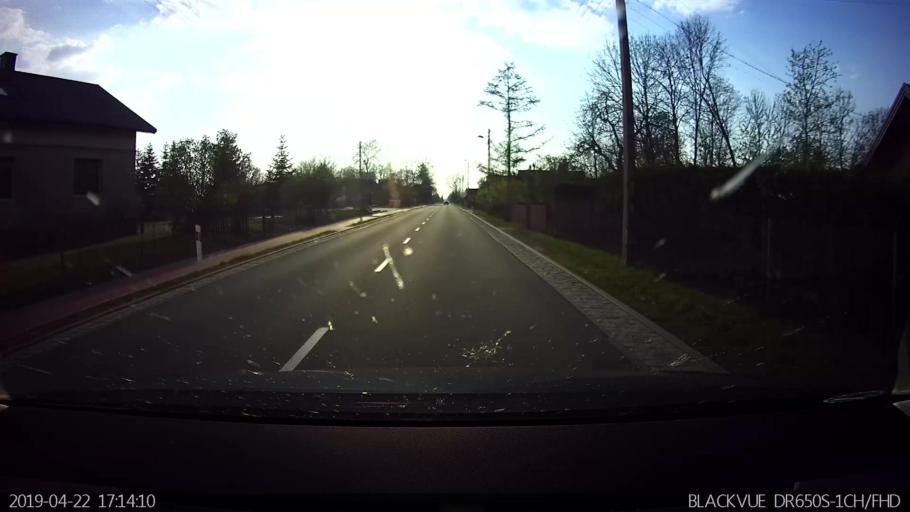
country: PL
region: Masovian Voivodeship
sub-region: Powiat sokolowski
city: Jablonna Lacka
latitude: 52.4013
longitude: 22.5067
